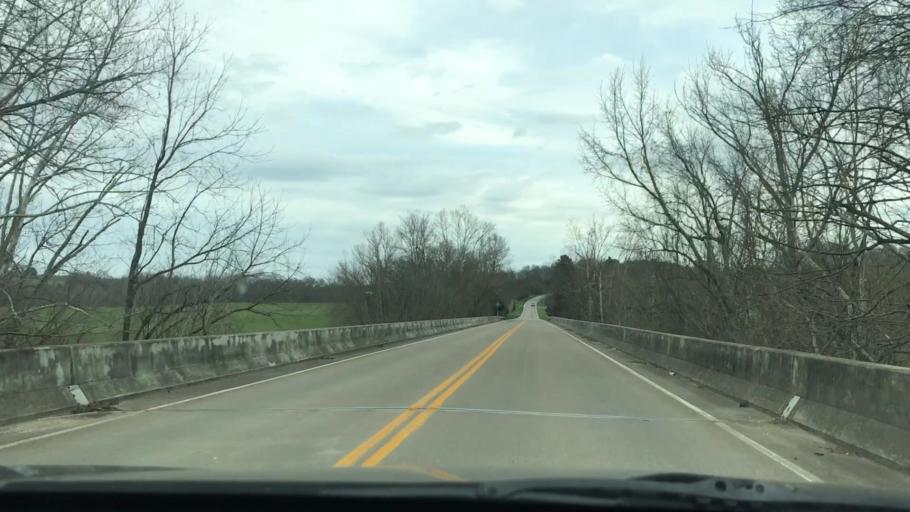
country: US
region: Kentucky
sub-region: Hart County
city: Munfordville
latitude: 37.3195
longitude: -85.7638
